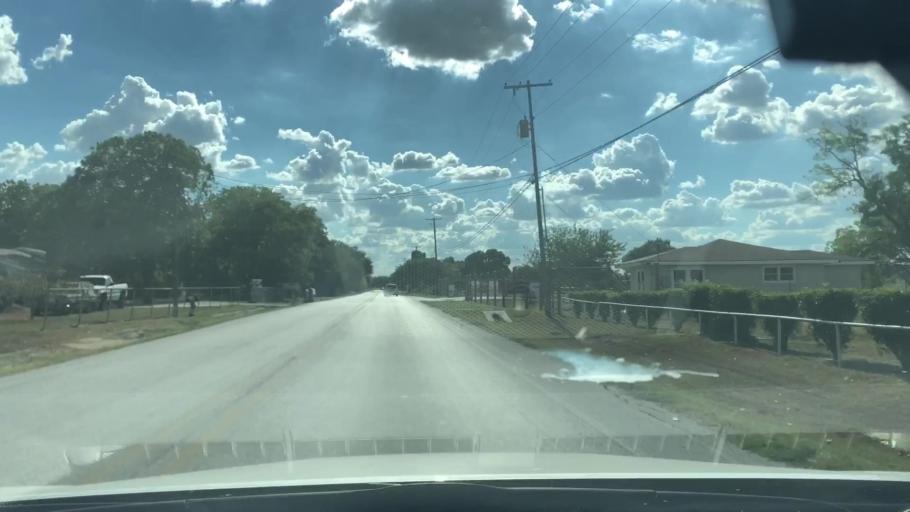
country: US
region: Texas
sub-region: Comal County
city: New Braunfels
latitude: 29.6643
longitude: -98.1764
